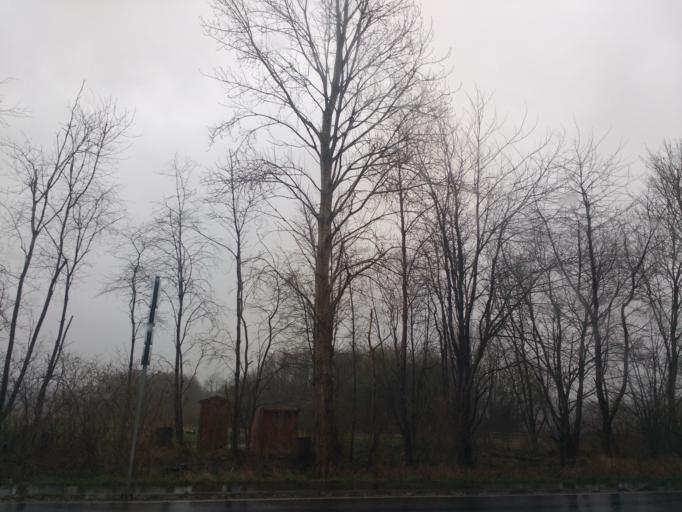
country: DE
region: Schleswig-Holstein
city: Wangels
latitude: 54.3041
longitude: 10.7733
